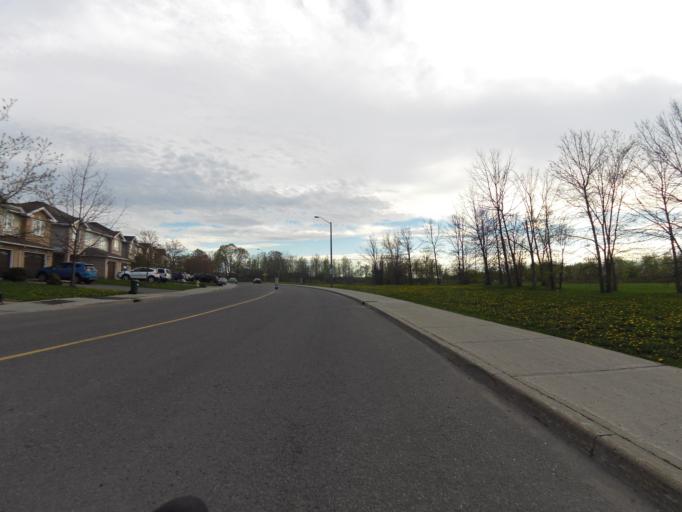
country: CA
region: Ontario
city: Bells Corners
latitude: 45.2837
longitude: -75.7380
